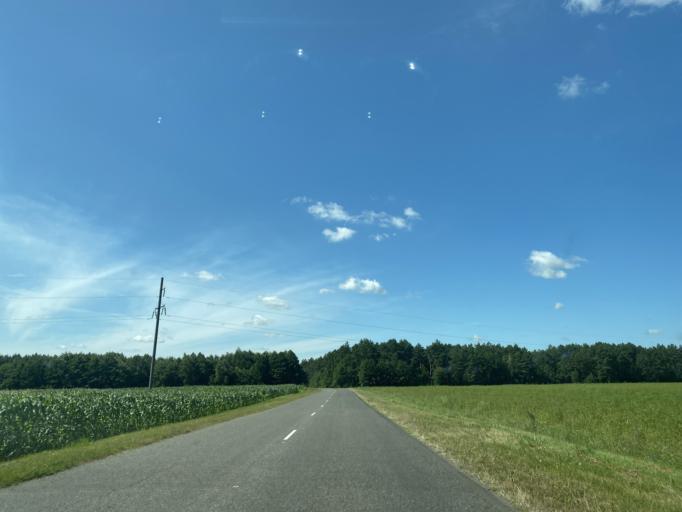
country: BY
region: Brest
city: Ivanava
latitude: 52.2266
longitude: 25.6389
